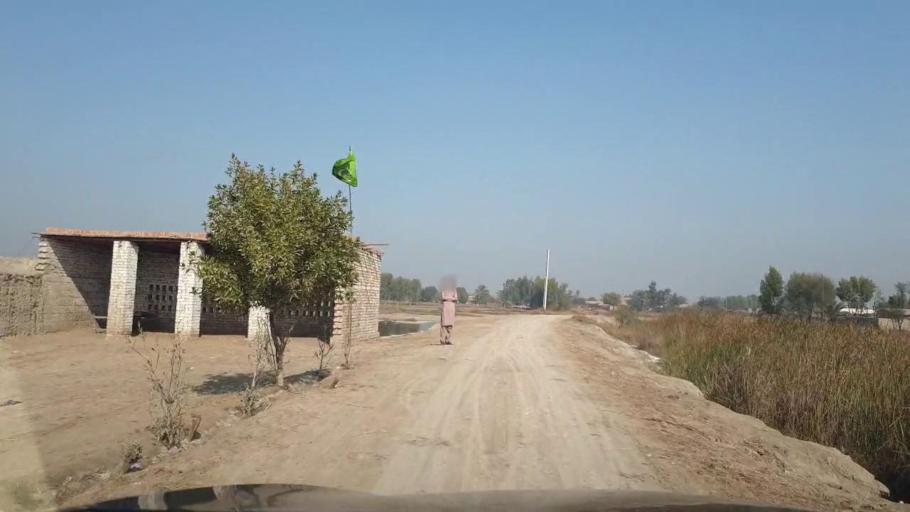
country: PK
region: Sindh
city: Ubauro
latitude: 28.1481
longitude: 69.7569
